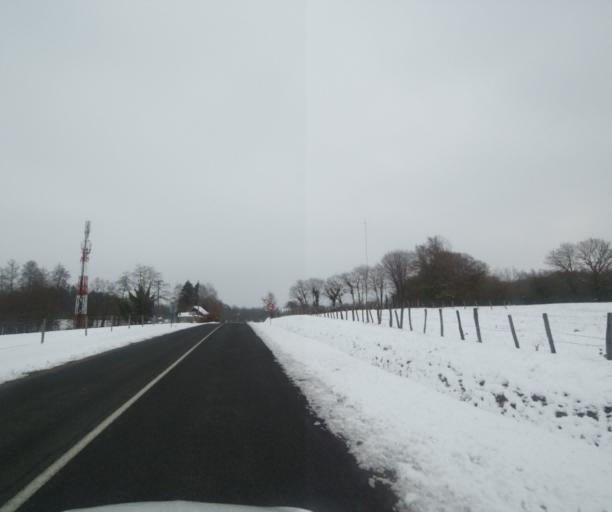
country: FR
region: Champagne-Ardenne
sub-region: Departement de la Haute-Marne
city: Villiers-en-Lieu
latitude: 48.6139
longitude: 4.8884
